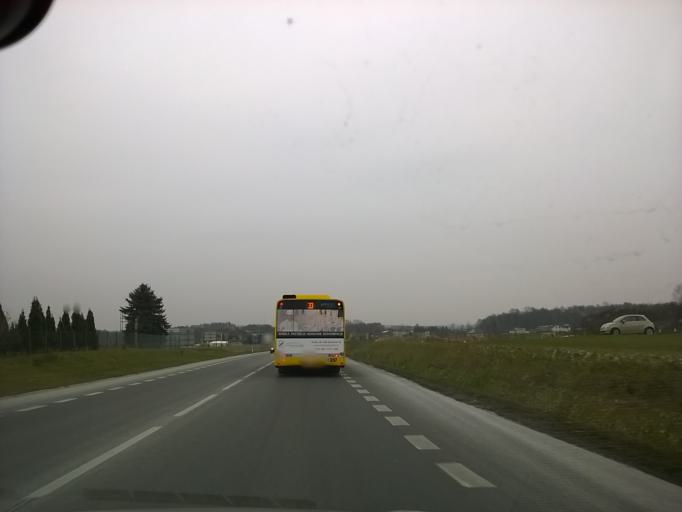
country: PL
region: Silesian Voivodeship
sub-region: Powiat gliwicki
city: Paniowki
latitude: 50.2321
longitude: 18.7928
